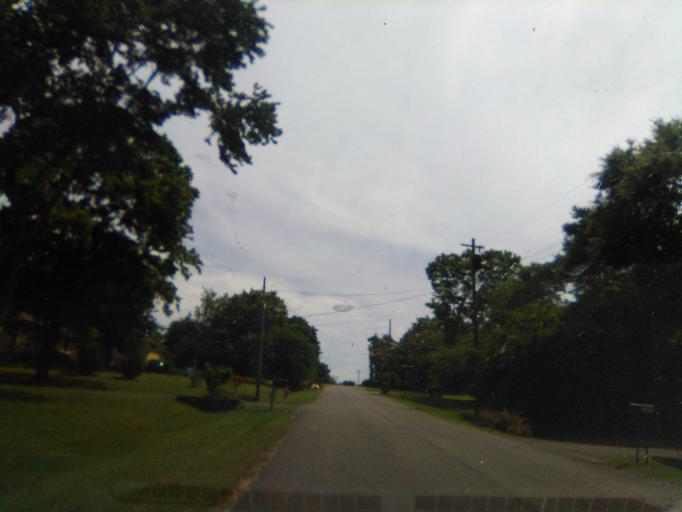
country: US
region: Tennessee
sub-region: Davidson County
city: Belle Meade
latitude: 36.1275
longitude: -86.8985
